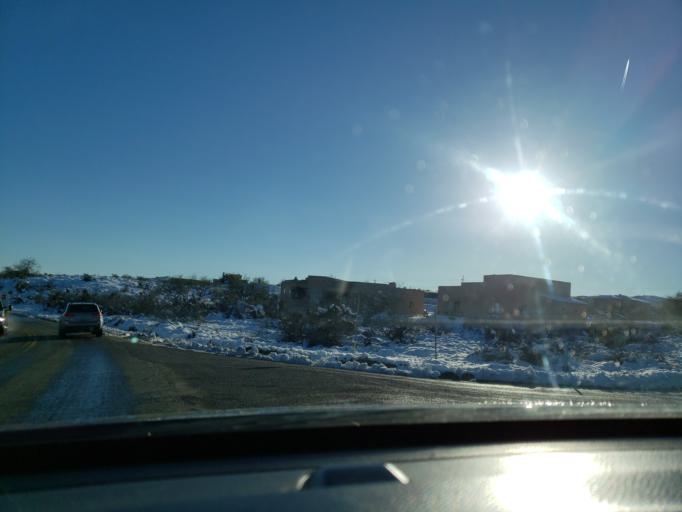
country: US
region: Arizona
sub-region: Maricopa County
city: Carefree
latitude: 33.8710
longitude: -111.8237
